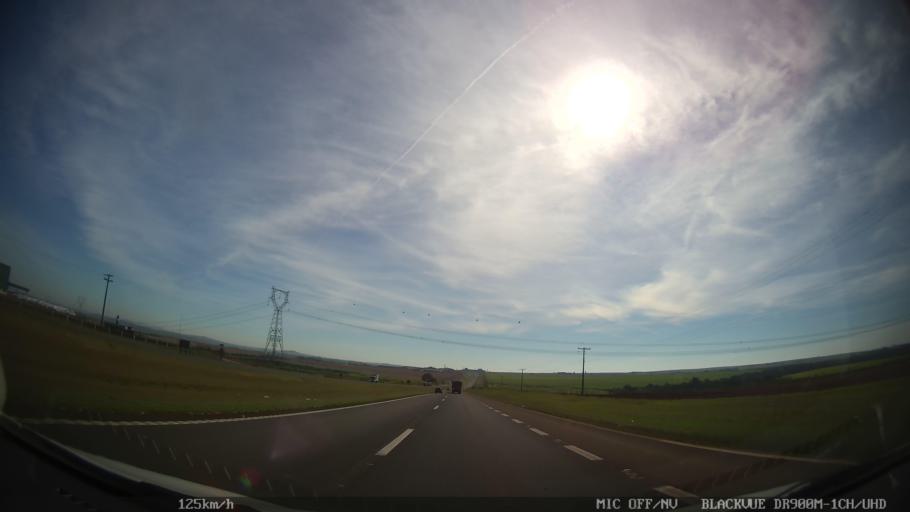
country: BR
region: Sao Paulo
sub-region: Cordeiropolis
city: Cordeiropolis
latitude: -22.4350
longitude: -47.3955
